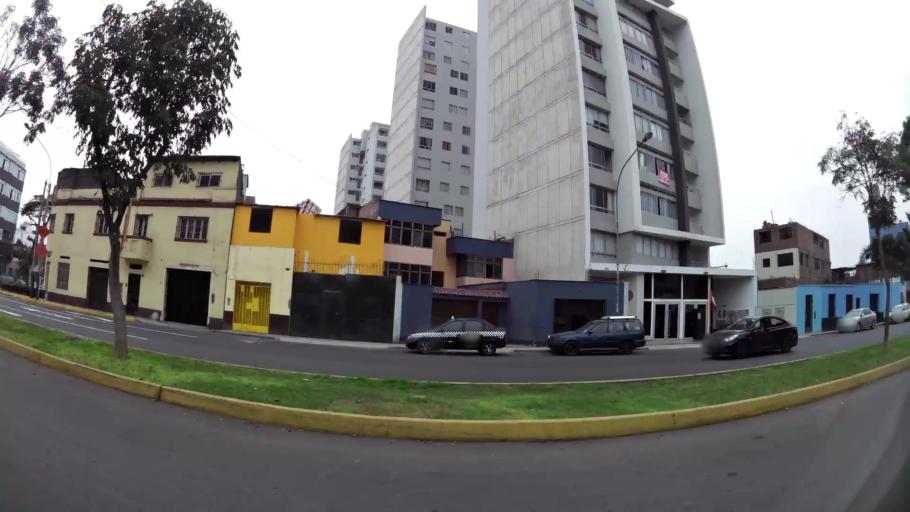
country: PE
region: Lima
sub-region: Lima
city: San Isidro
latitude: -12.0897
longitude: -77.0295
